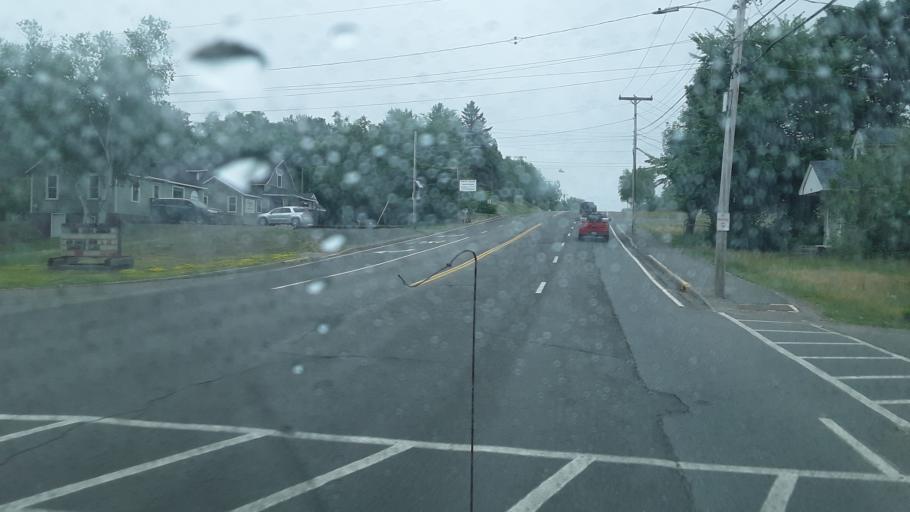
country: US
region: Maine
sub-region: Penobscot County
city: Millinocket
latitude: 45.6574
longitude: -68.7033
